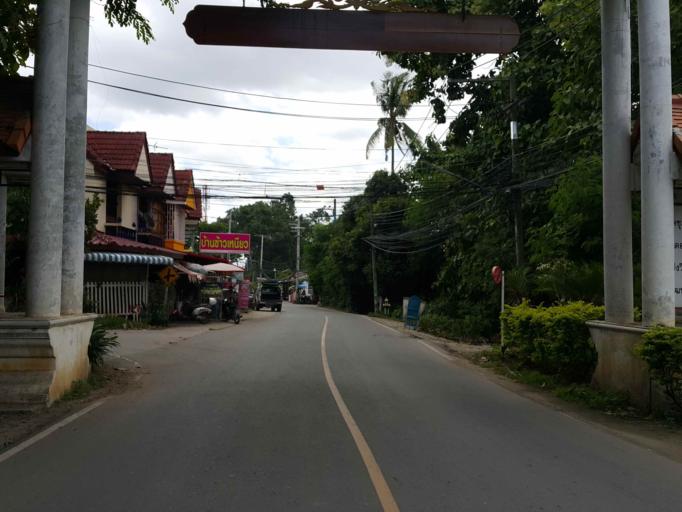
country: TH
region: Chiang Mai
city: Chiang Mai
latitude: 18.8266
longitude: 98.9989
